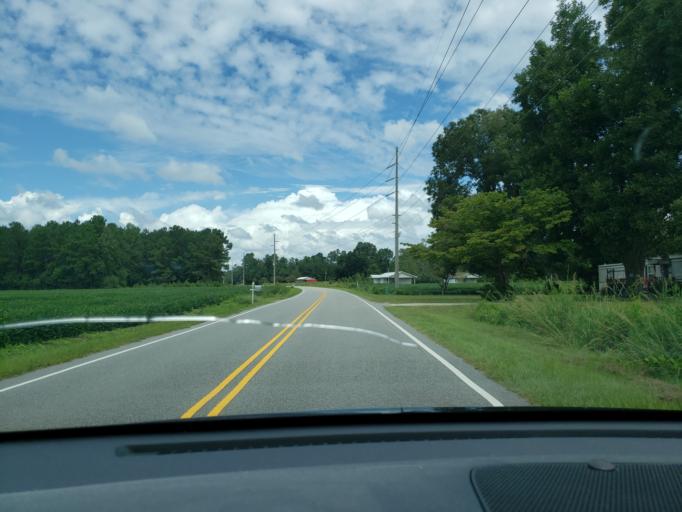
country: US
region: North Carolina
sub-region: Columbus County
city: Tabor City
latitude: 34.1645
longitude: -78.7821
